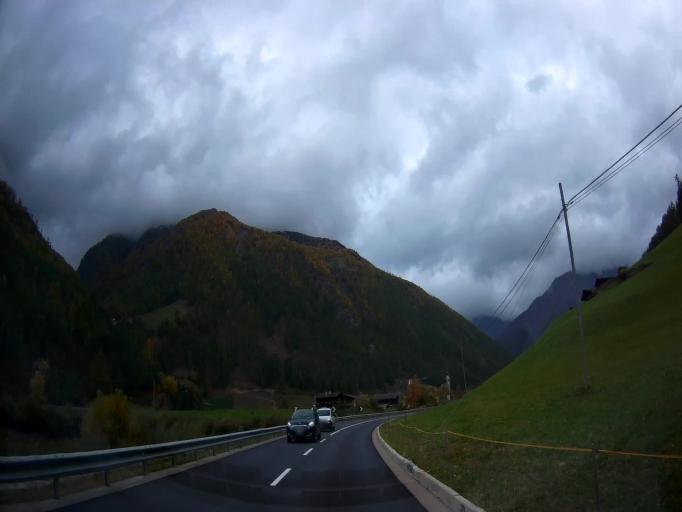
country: IT
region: Trentino-Alto Adige
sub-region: Bolzano
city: Senales
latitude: 46.7186
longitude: 10.8670
